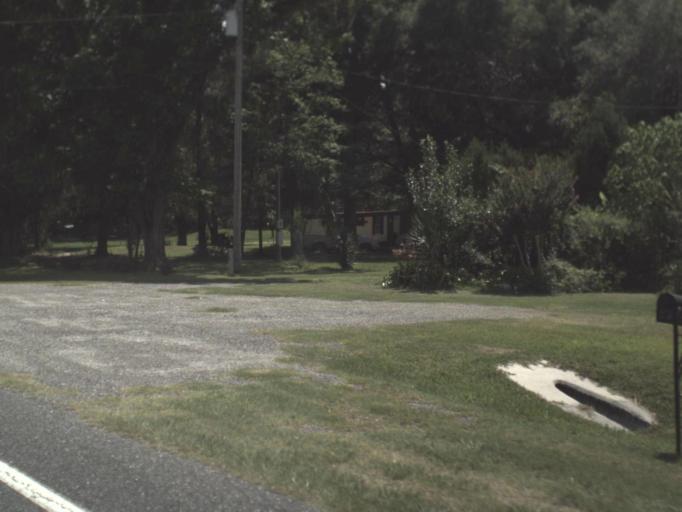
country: US
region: Florida
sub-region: Alachua County
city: High Springs
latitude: 29.9592
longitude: -82.6040
